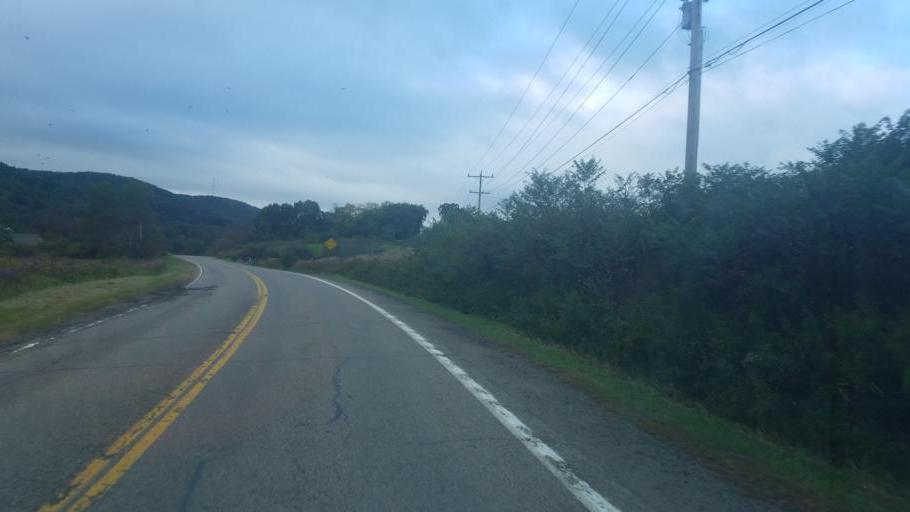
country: US
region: New York
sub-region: Allegany County
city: Cuba
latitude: 42.1850
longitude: -78.3579
